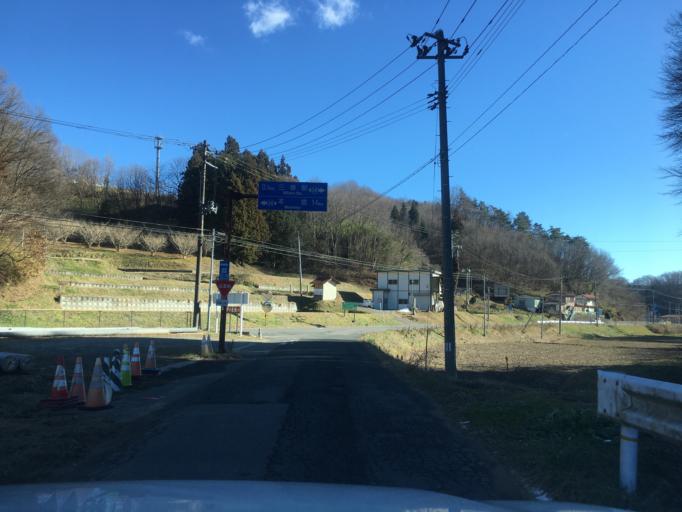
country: JP
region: Fukushima
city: Miharu
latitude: 37.4534
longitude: 140.4715
